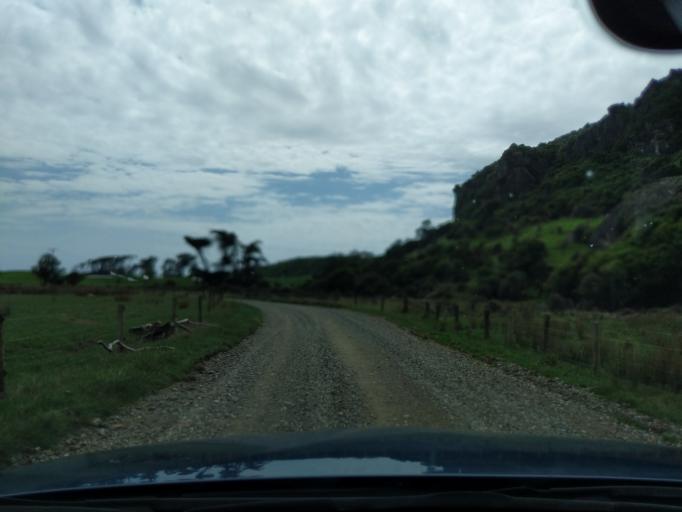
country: NZ
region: Tasman
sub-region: Tasman District
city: Takaka
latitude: -40.6471
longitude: 172.4380
